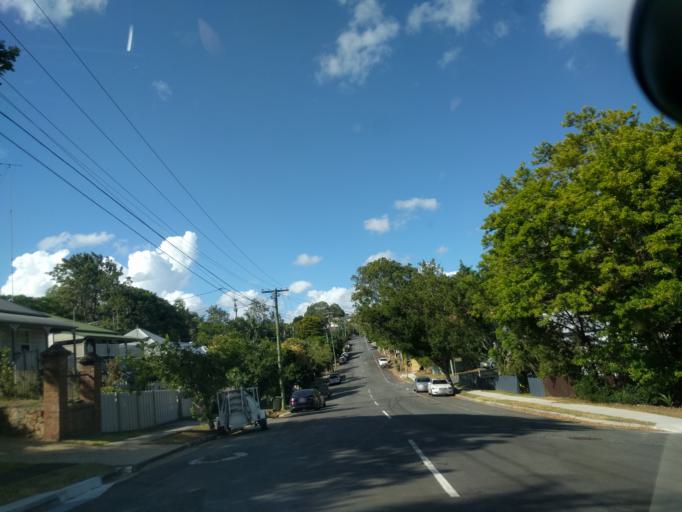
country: AU
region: Queensland
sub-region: Brisbane
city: Milton
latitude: -27.4567
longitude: 153.0037
